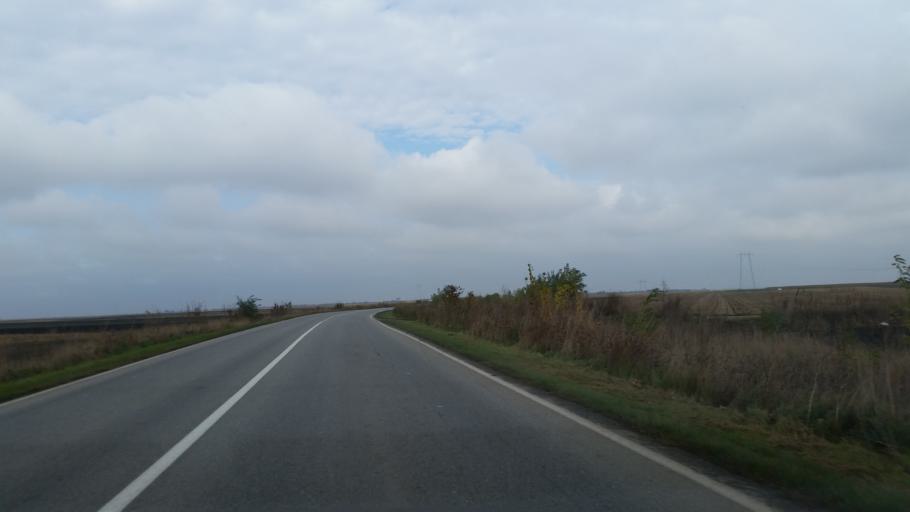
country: RS
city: Melenci
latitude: 45.4829
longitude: 20.3346
